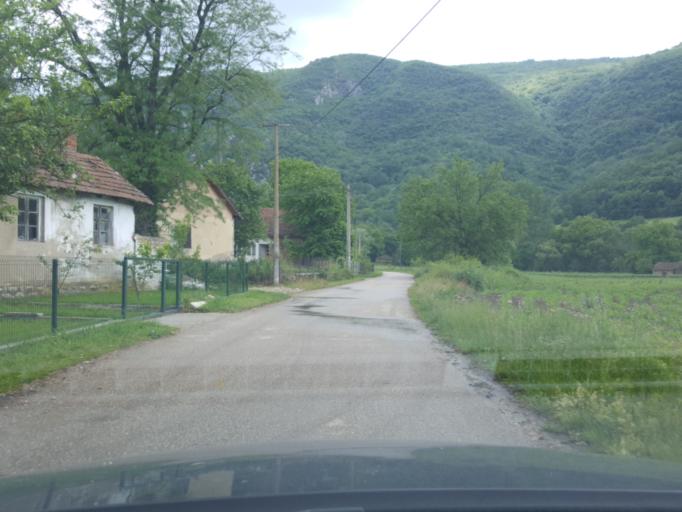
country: RS
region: Central Serbia
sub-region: Zajecarski Okrug
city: Soko Banja
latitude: 43.6343
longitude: 21.9890
